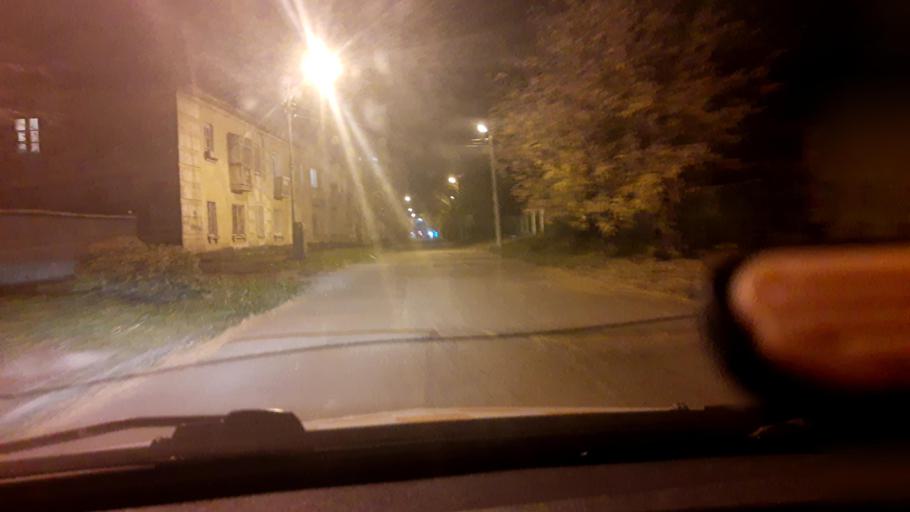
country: RU
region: Bashkortostan
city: Ufa
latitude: 54.8237
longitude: 56.0903
